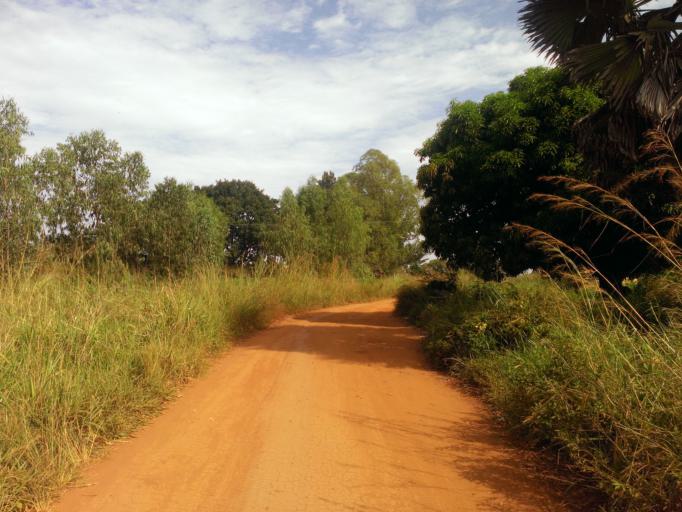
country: UG
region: Northern Region
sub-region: Gulu District
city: Gulu
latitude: 2.7870
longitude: 32.3181
